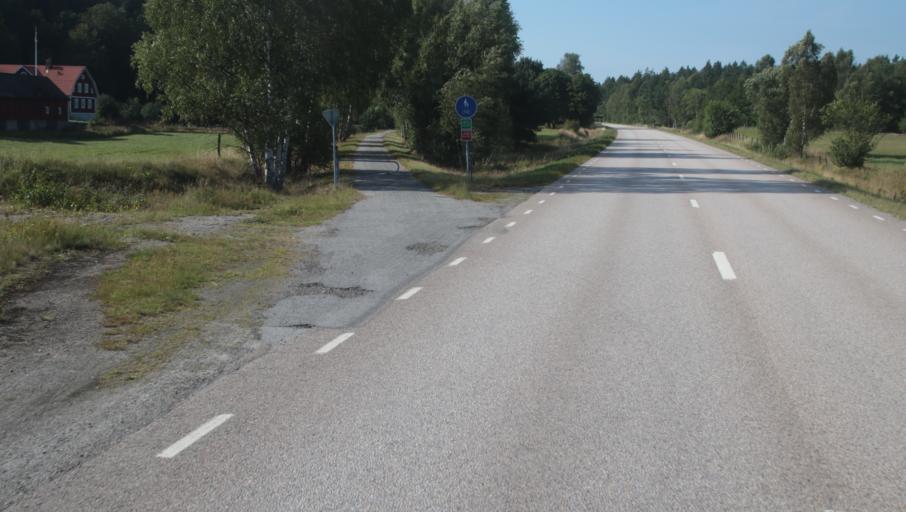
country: SE
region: Blekinge
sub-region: Karlshamns Kommun
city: Svangsta
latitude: 56.2979
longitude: 14.7361
